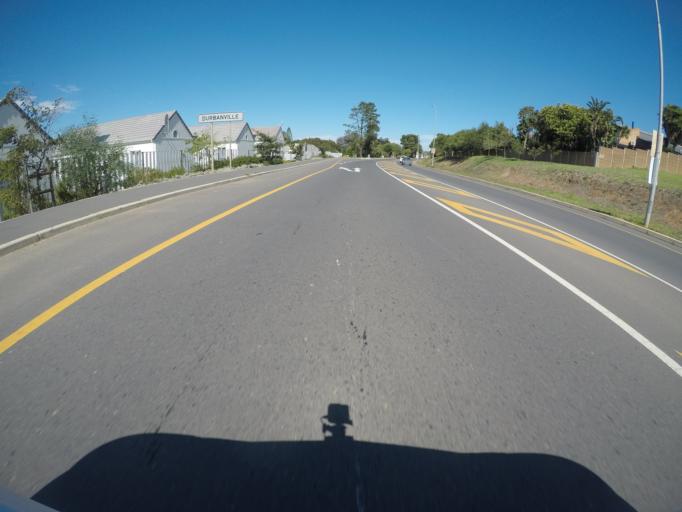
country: ZA
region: Western Cape
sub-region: City of Cape Town
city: Kraaifontein
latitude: -33.8240
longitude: 18.6369
